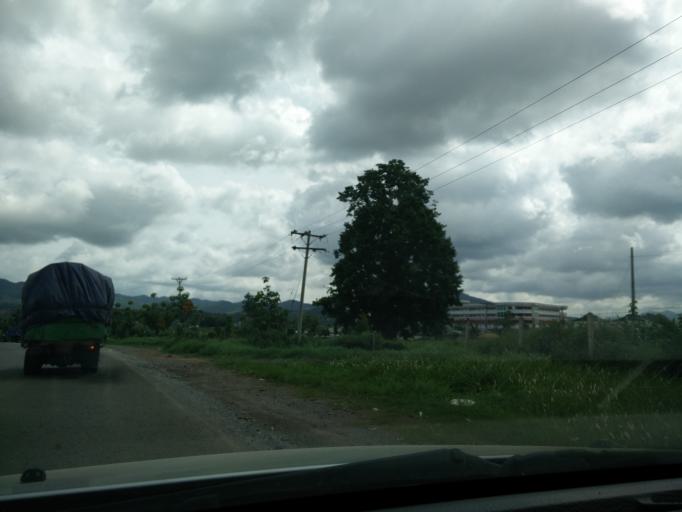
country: MM
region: Shan
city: Lashio
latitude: 23.0285
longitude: 97.7710
